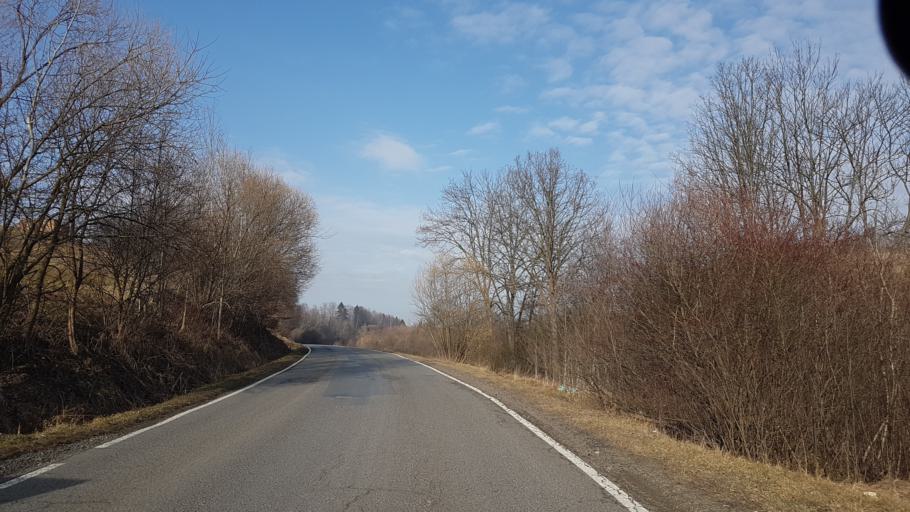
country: PL
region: Lesser Poland Voivodeship
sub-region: Powiat limanowski
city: Lukowica
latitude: 49.6237
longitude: 20.5109
